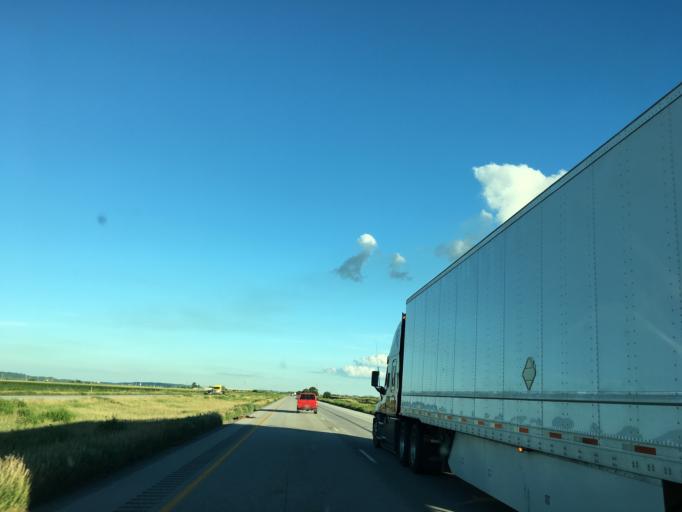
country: US
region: Iowa
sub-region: Fremont County
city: Hamburg
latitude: 40.6515
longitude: -95.7493
